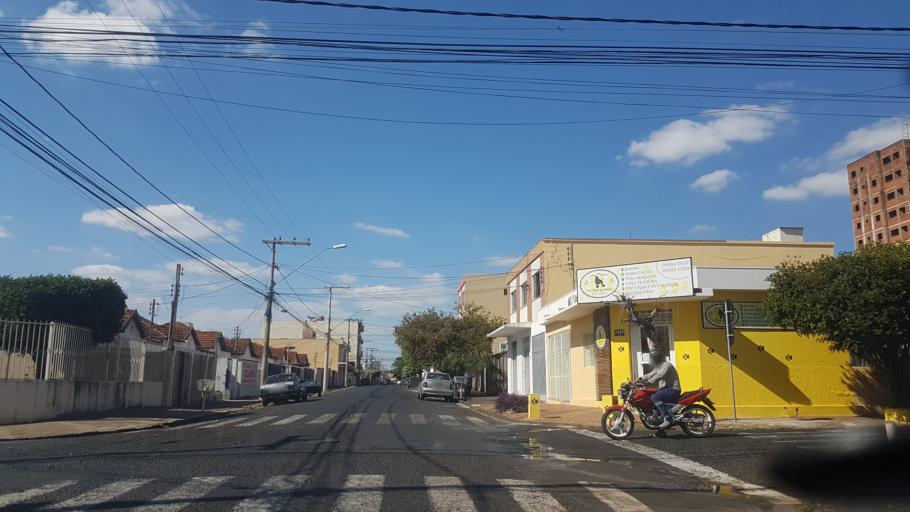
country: BR
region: Minas Gerais
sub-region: Uberlandia
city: Uberlandia
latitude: -18.9075
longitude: -48.2810
